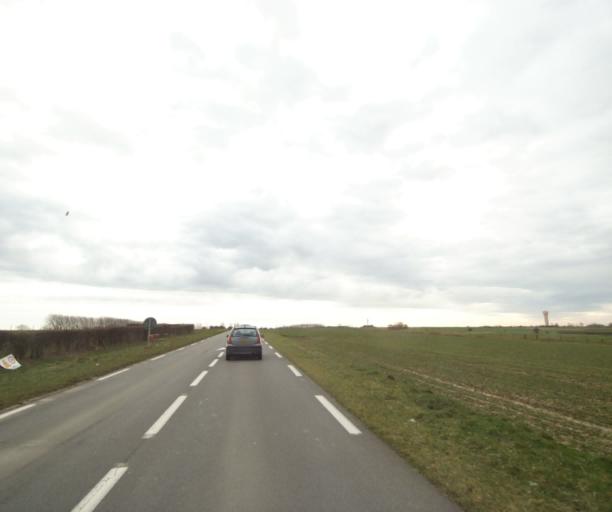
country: FR
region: Nord-Pas-de-Calais
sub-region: Departement du Nord
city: Curgies
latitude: 50.3242
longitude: 3.6133
